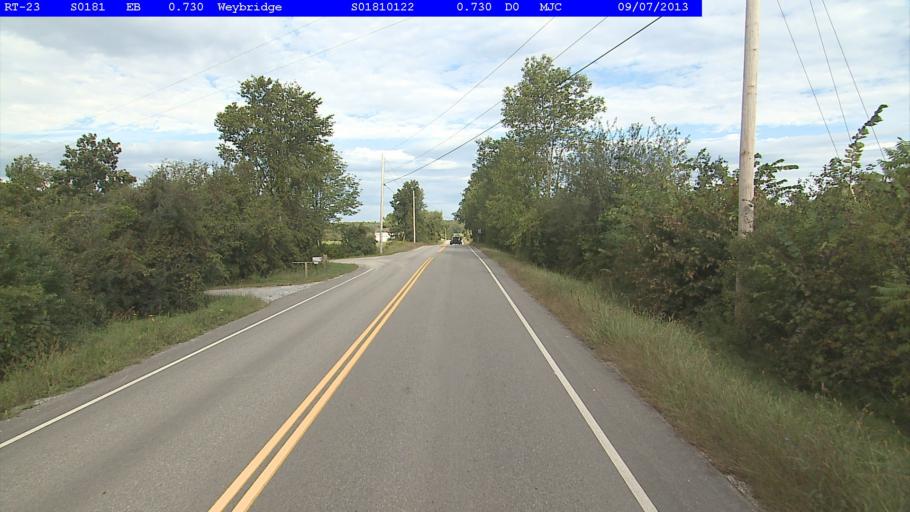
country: US
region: Vermont
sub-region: Addison County
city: Middlebury (village)
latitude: 44.0253
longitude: -73.1941
